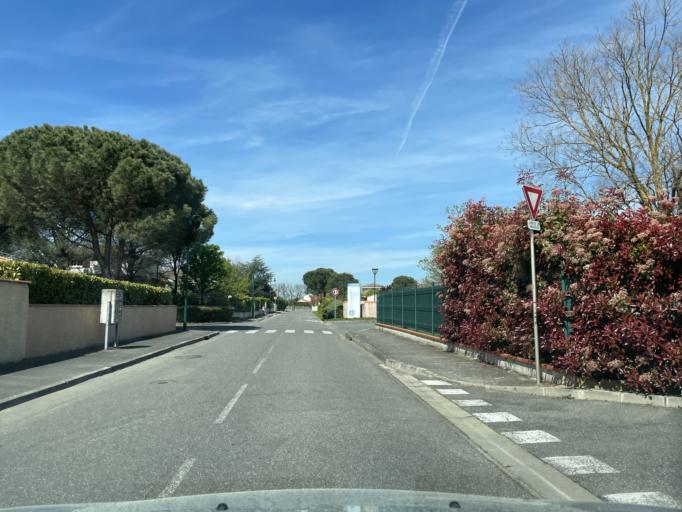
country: FR
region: Midi-Pyrenees
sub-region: Departement de la Haute-Garonne
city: Pibrac
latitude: 43.6152
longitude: 1.2696
